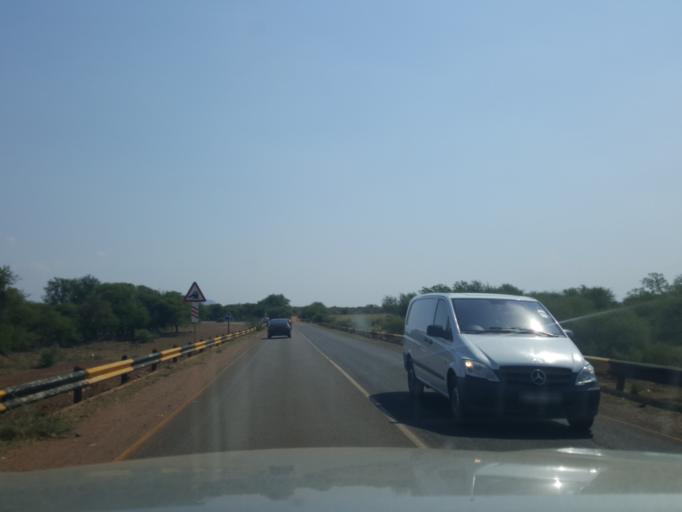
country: BW
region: South East
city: Ramotswa
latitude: -24.8502
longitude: 25.8296
